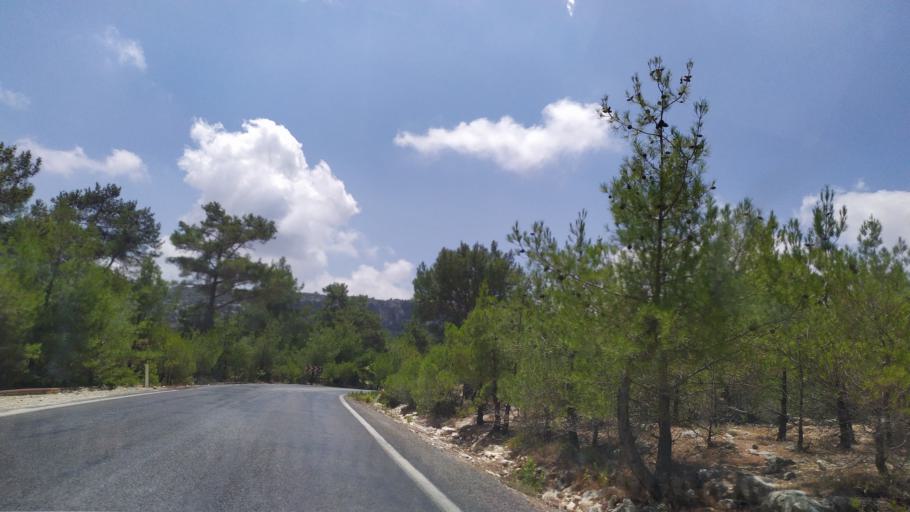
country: TR
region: Mersin
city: Gulnar
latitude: 36.2765
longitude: 33.3880
